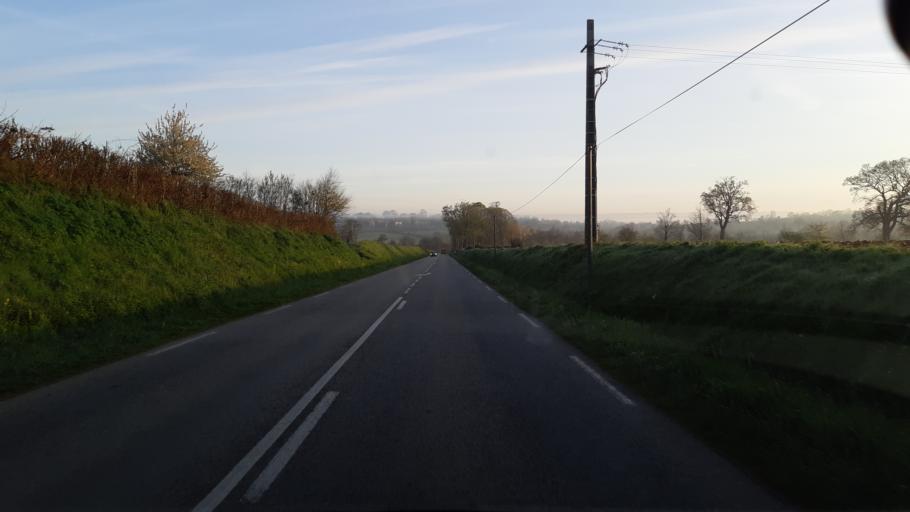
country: FR
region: Lower Normandy
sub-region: Departement de la Manche
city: Agneaux
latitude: 49.0614
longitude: -1.1329
